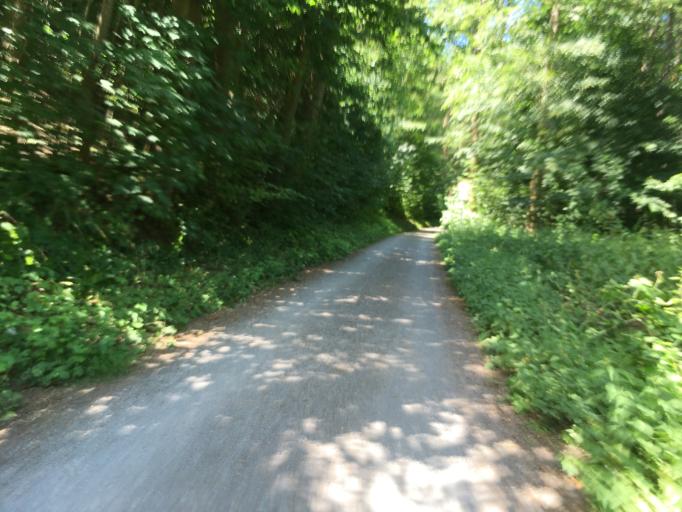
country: DE
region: Baden-Wuerttemberg
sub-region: Regierungsbezirk Stuttgart
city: Vaihingen an der Enz
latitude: 48.9147
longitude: 8.9618
